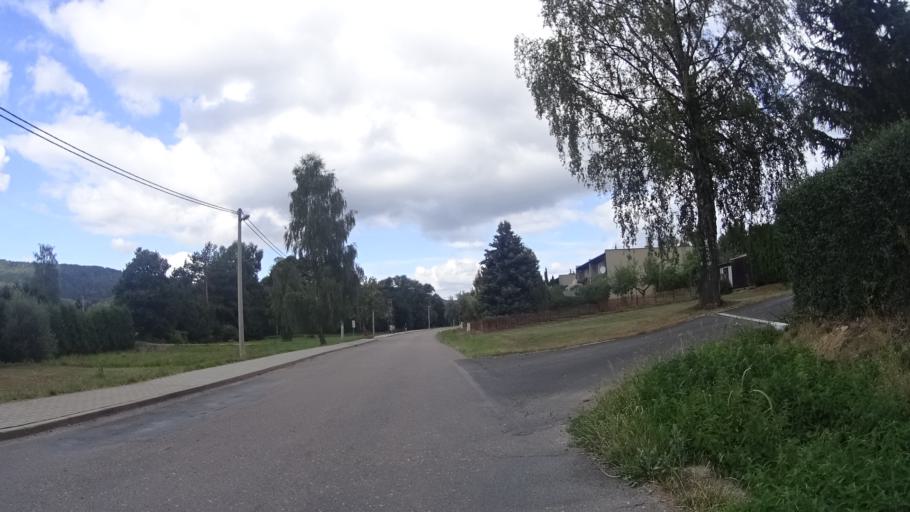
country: CZ
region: Pardubicky
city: Dolni Cermna
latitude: 49.9308
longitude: 16.5394
